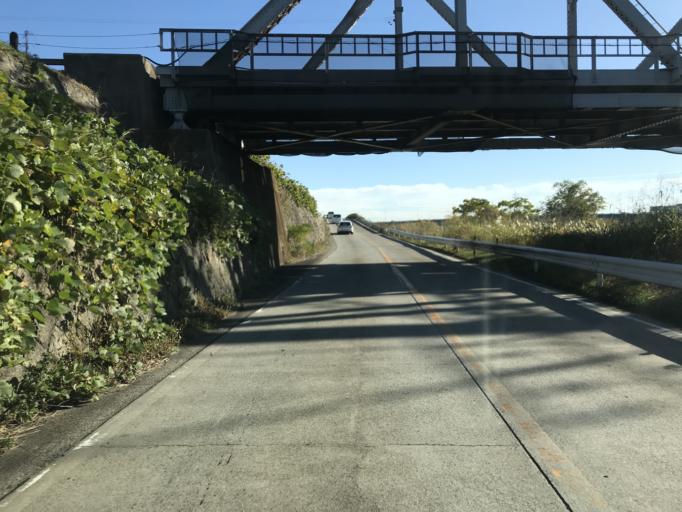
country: JP
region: Aichi
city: Kanie
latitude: 35.1436
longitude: 136.8336
